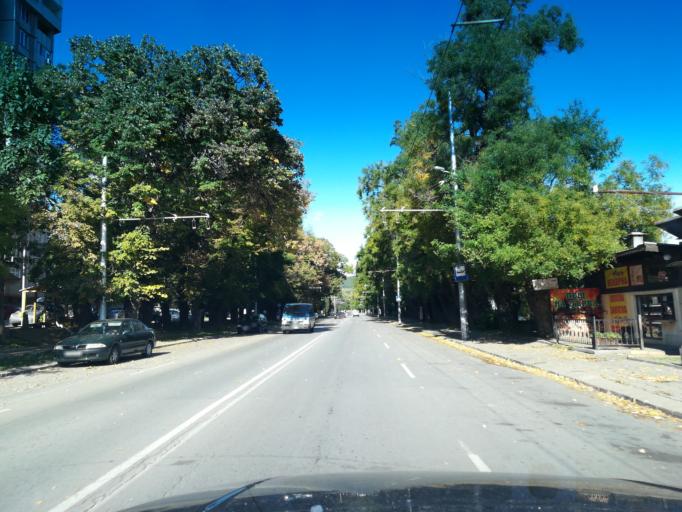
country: BG
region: Stara Zagora
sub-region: Obshtina Stara Zagora
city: Stara Zagora
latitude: 42.4394
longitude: 25.6324
